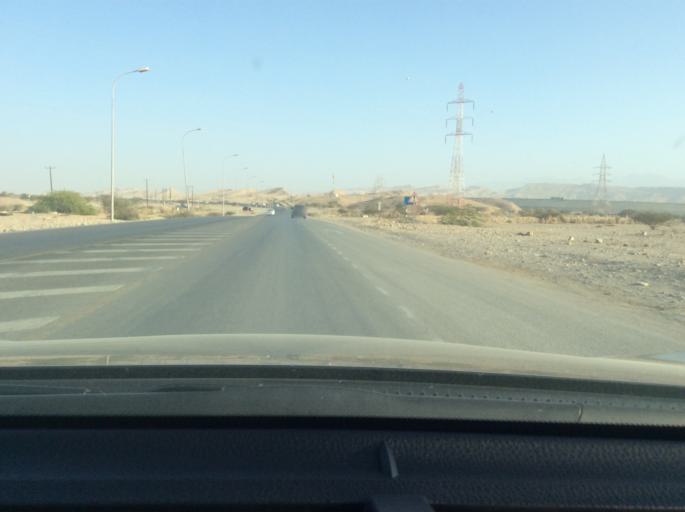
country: OM
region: Muhafazat Masqat
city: As Sib al Jadidah
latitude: 23.5749
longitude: 58.1843
